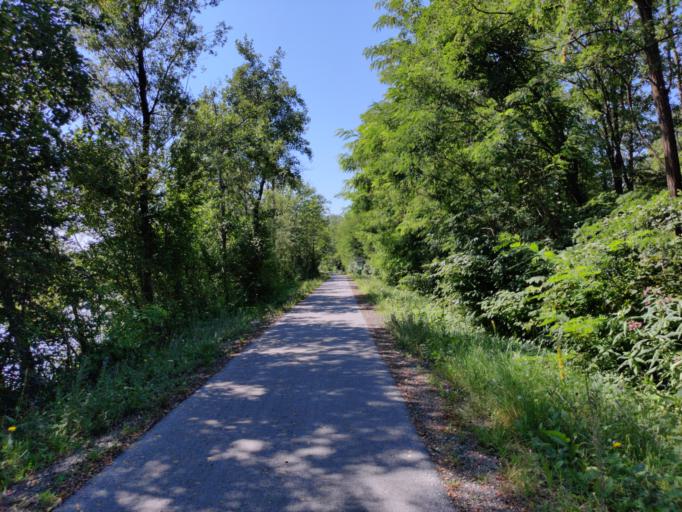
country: AT
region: Styria
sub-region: Politischer Bezirk Leibnitz
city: Stocking
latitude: 46.8675
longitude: 15.5310
